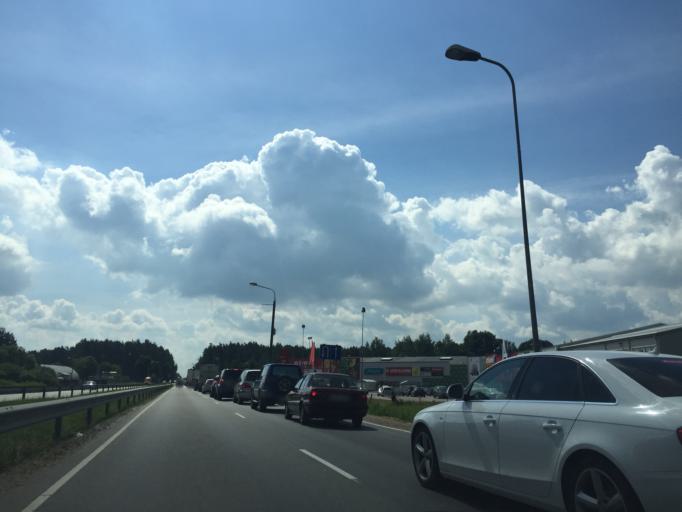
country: LV
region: Kekava
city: Balozi
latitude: 56.8974
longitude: 24.1383
